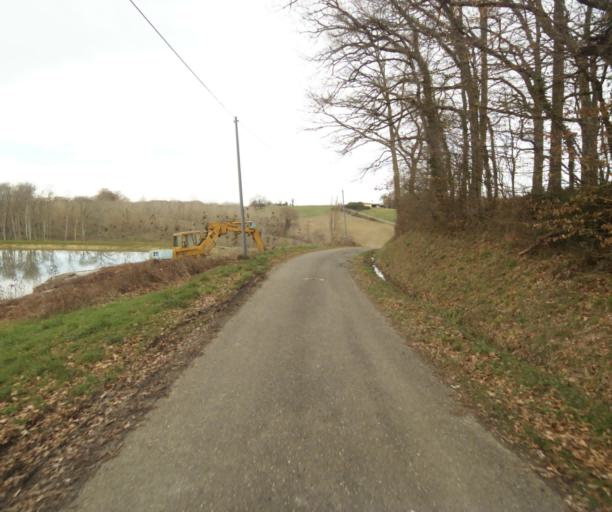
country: FR
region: Midi-Pyrenees
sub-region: Departement du Gers
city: Eauze
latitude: 43.9110
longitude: 0.0508
